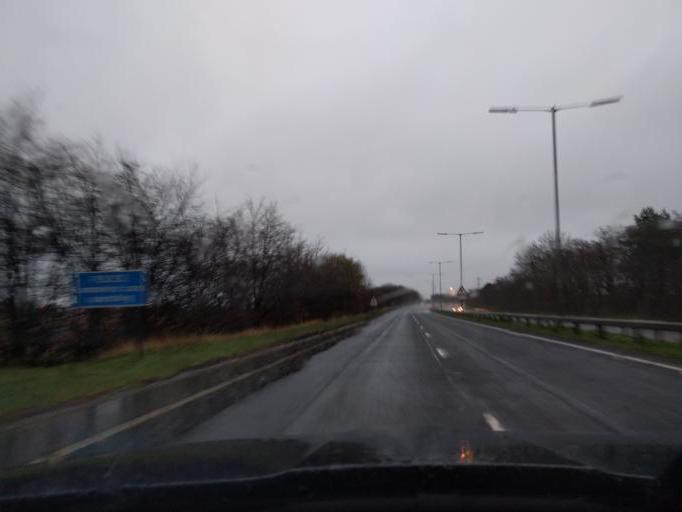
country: GB
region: England
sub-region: Northumberland
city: Newbiggin-by-the-Sea
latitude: 55.1812
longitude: -1.5342
